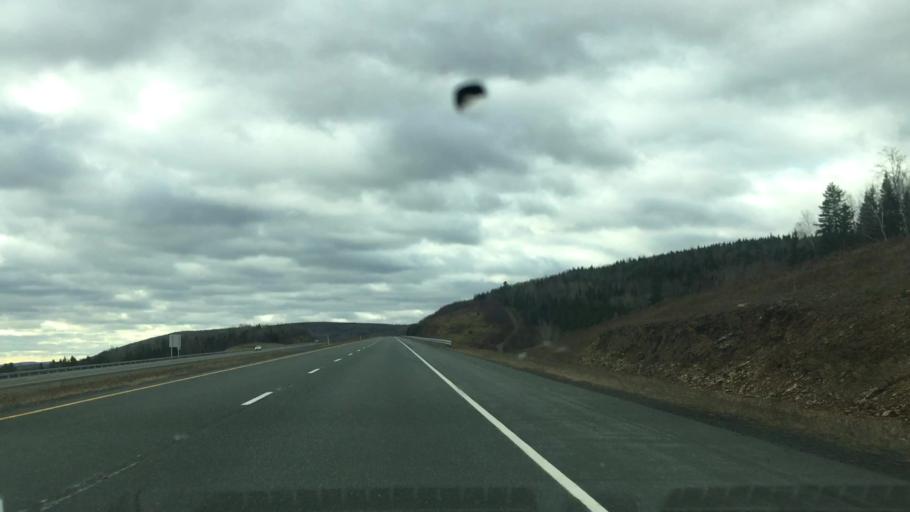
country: US
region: Maine
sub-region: Aroostook County
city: Fort Fairfield
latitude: 46.7216
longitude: -67.7307
